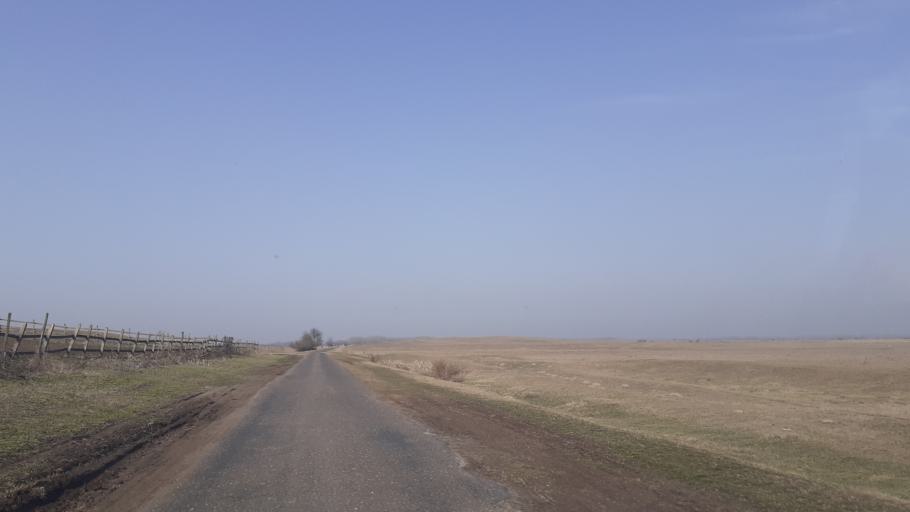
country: HU
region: Pest
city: Dabas
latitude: 47.0958
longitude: 19.2316
